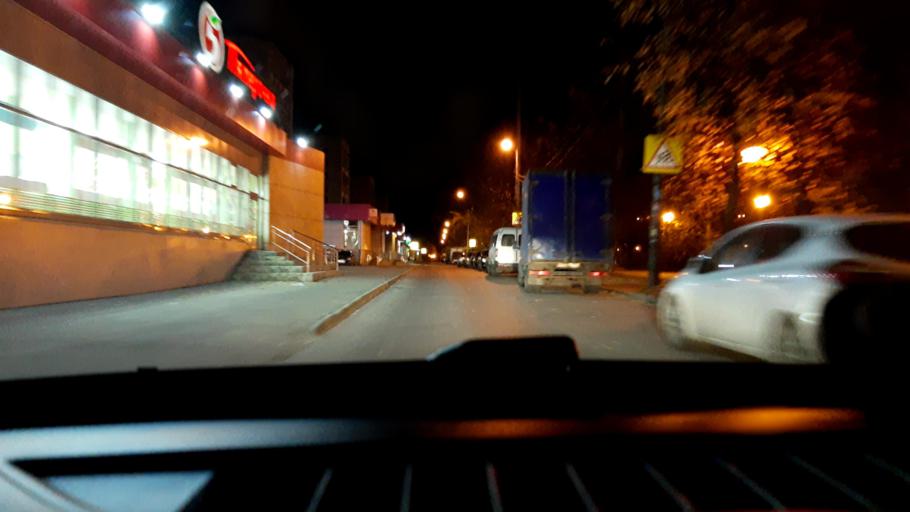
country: RU
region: Nizjnij Novgorod
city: Nizhniy Novgorod
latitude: 56.2638
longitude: 43.8862
